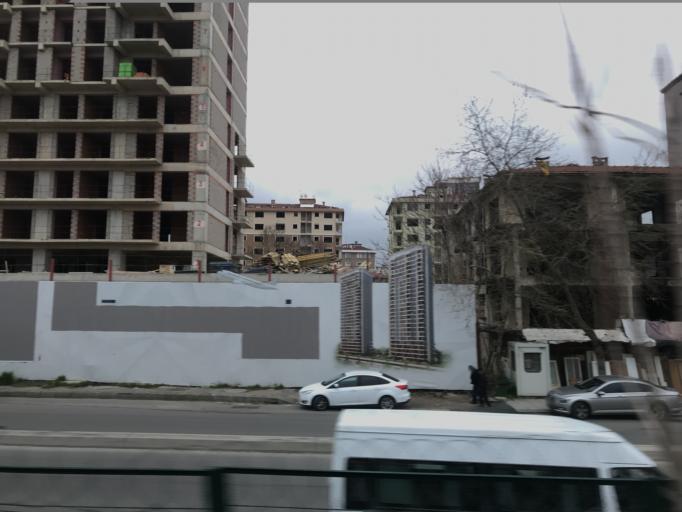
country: TR
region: Istanbul
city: Maltepe
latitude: 40.9045
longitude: 29.1630
